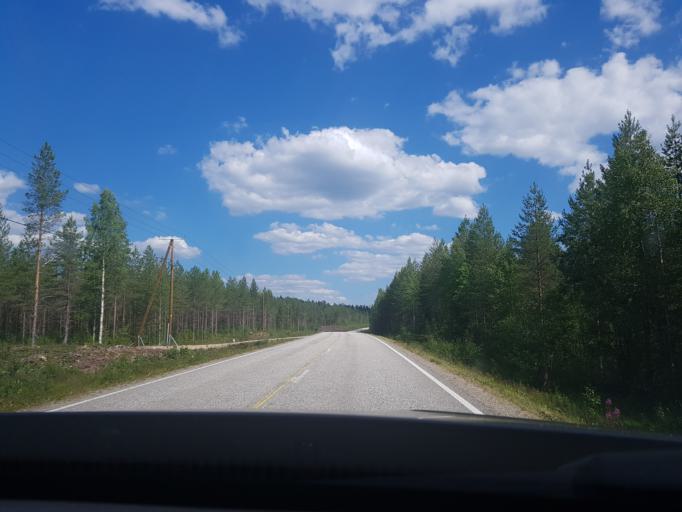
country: FI
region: Kainuu
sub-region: Kehys-Kainuu
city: Kuhmo
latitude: 64.2052
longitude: 29.7212
